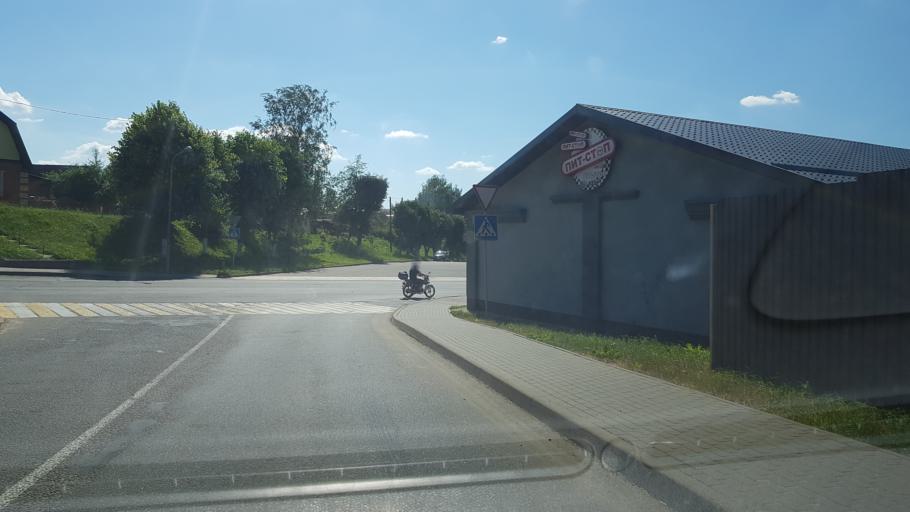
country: BY
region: Vitebsk
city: Orsha
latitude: 54.5058
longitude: 30.4330
